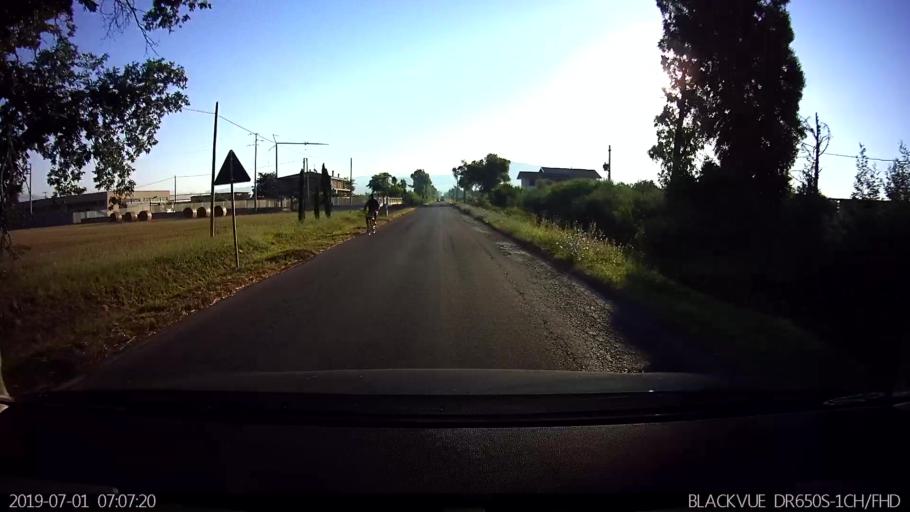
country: IT
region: Latium
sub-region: Provincia di Latina
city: Borgo Hermada
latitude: 41.2881
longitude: 13.1378
